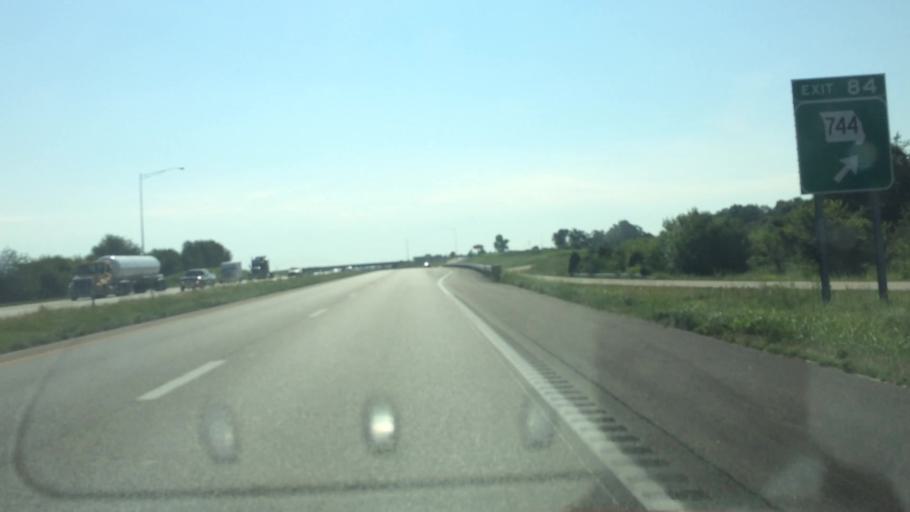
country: US
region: Missouri
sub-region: Greene County
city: Strafford
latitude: 37.2500
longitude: -93.1900
